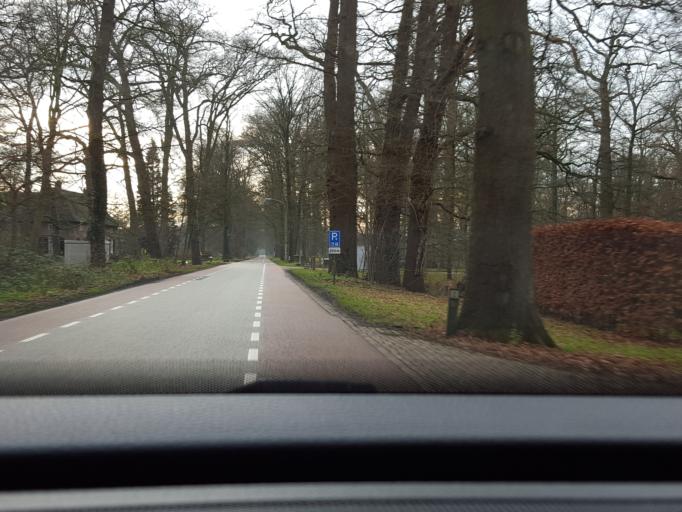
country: NL
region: Gelderland
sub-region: Gemeente Zutphen
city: Leesten
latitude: 52.1008
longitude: 6.2805
